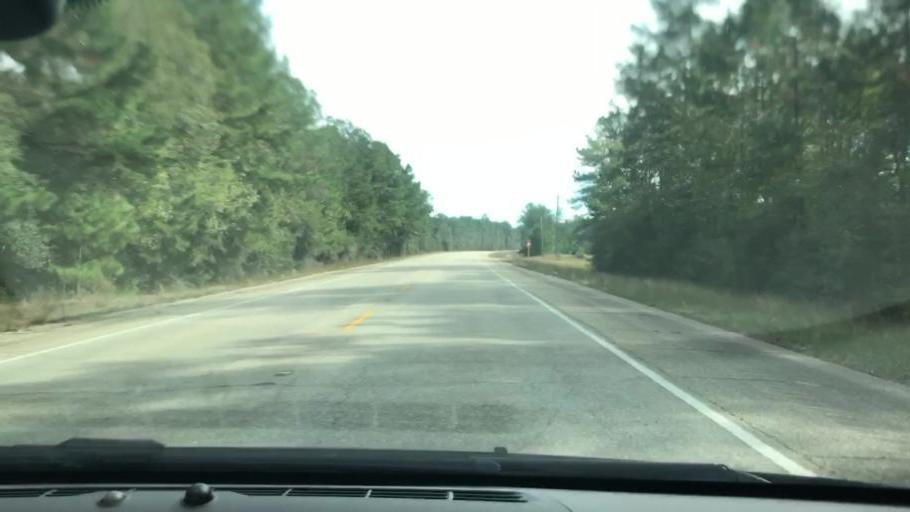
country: US
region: Mississippi
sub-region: Pearl River County
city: Nicholson
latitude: 30.5215
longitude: -89.8455
